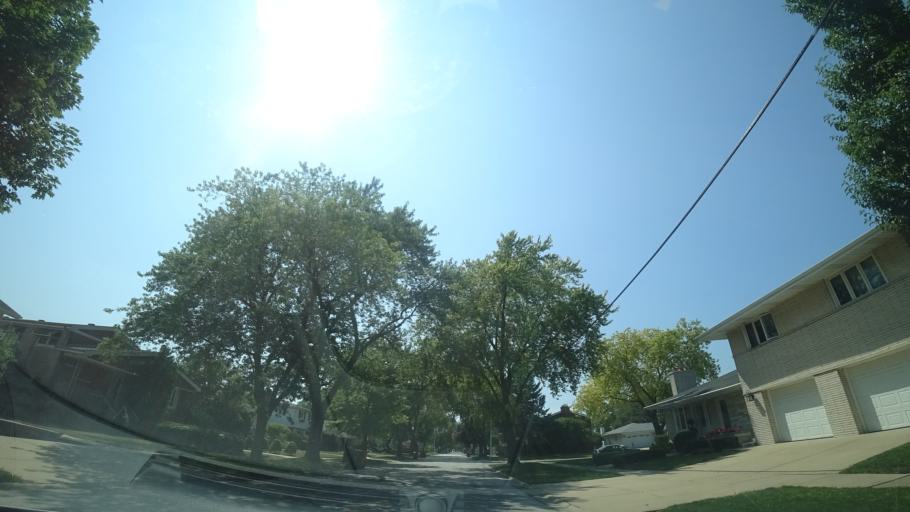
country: US
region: Illinois
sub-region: Cook County
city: Oak Lawn
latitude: 41.7018
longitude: -87.7481
